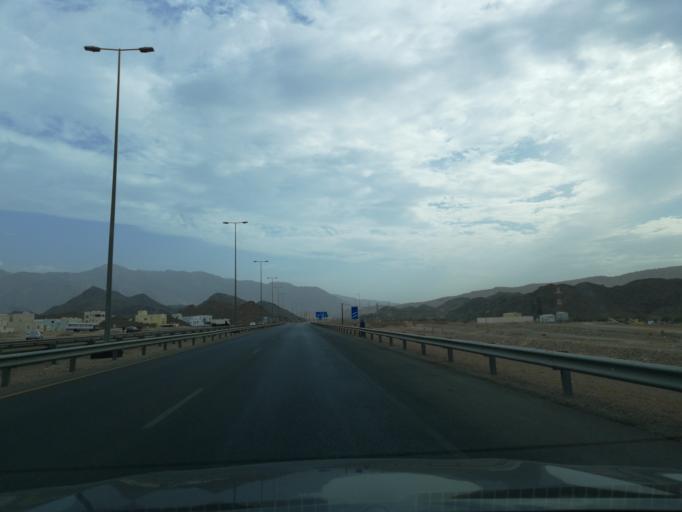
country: OM
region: Muhafazat Masqat
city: Bawshar
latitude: 23.5058
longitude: 58.3358
